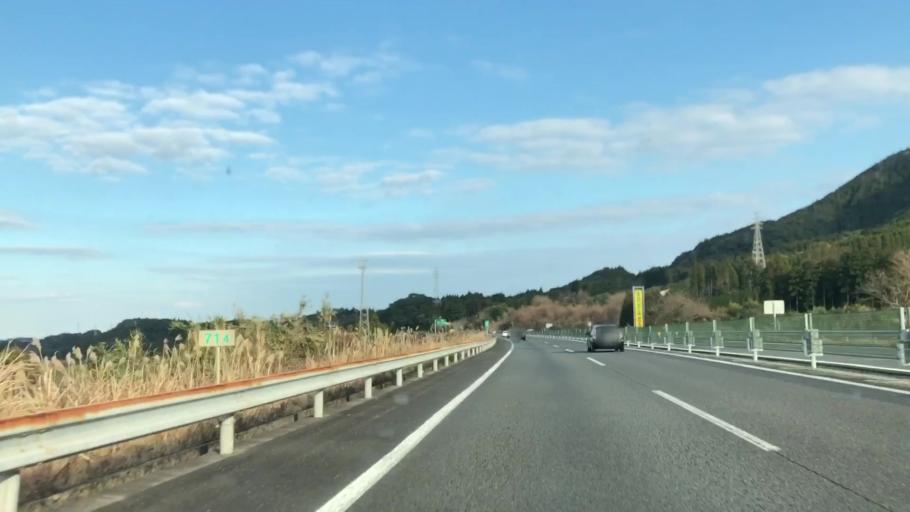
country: JP
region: Miyazaki
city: Miyazaki-shi
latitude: 31.8333
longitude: 131.3357
